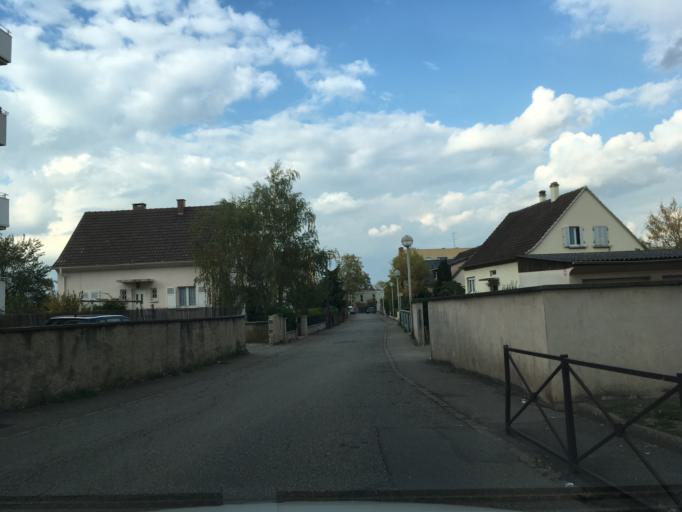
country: FR
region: Alsace
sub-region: Departement du Haut-Rhin
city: Ingersheim
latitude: 48.0876
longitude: 7.3273
